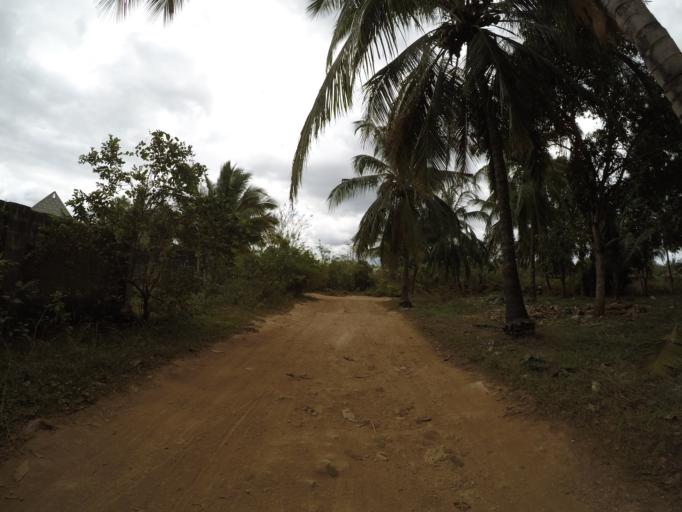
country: TZ
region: Zanzibar Central/South
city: Koani
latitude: -6.1932
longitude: 39.3066
